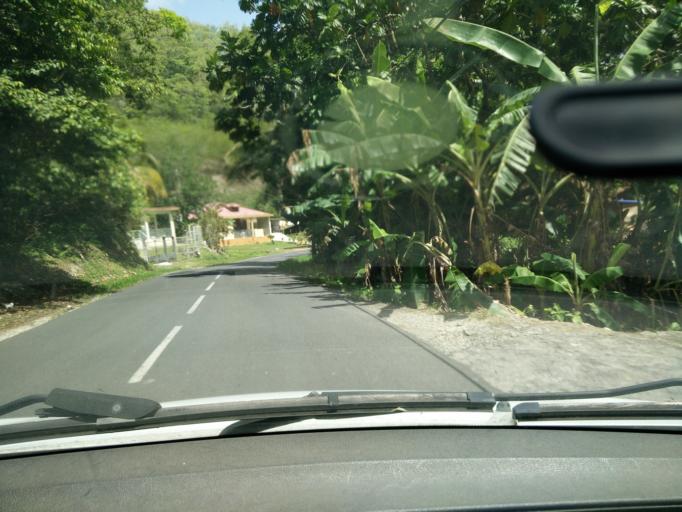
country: GP
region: Guadeloupe
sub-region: Guadeloupe
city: Les Abymes
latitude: 16.2910
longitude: -61.4566
